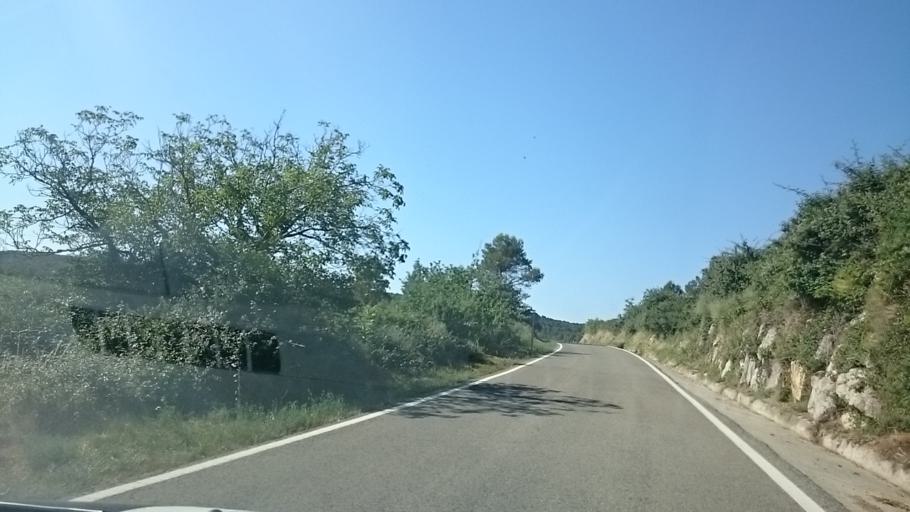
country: ES
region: Catalonia
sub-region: Provincia de Tarragona
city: Querol
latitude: 41.4002
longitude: 1.4717
